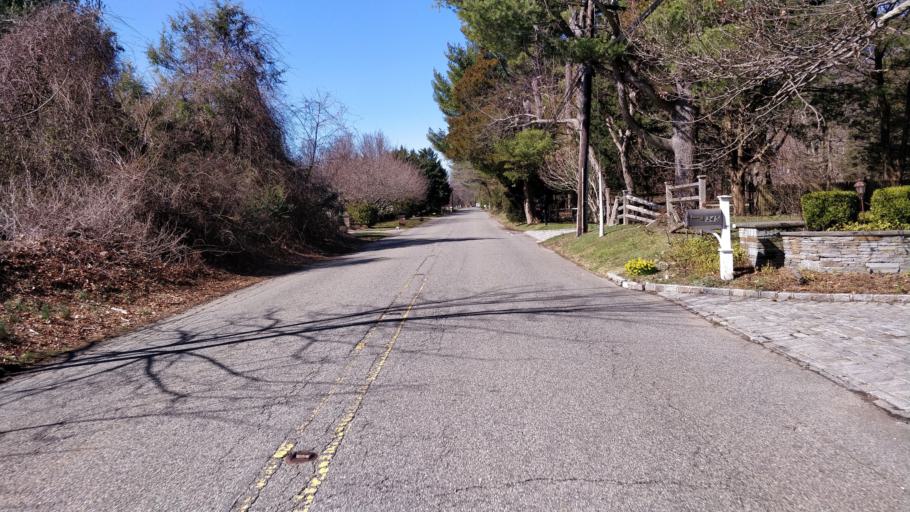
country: US
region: New York
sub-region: Nassau County
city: Woodbury
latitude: 40.8383
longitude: -73.4772
